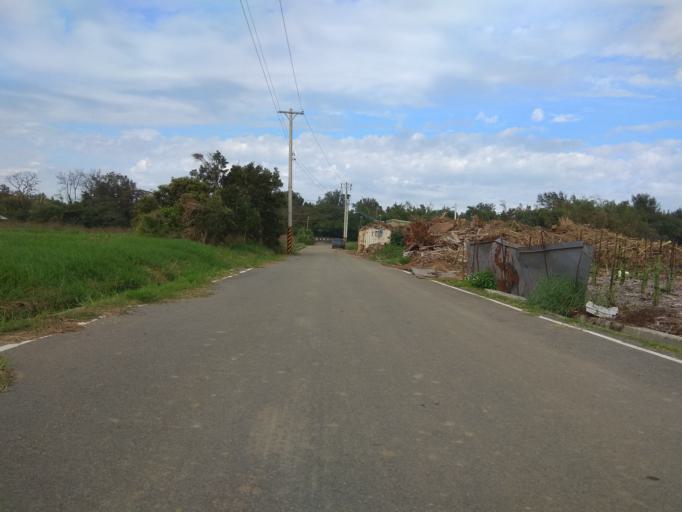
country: TW
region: Taiwan
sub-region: Hsinchu
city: Zhubei
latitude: 24.9608
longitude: 121.0067
